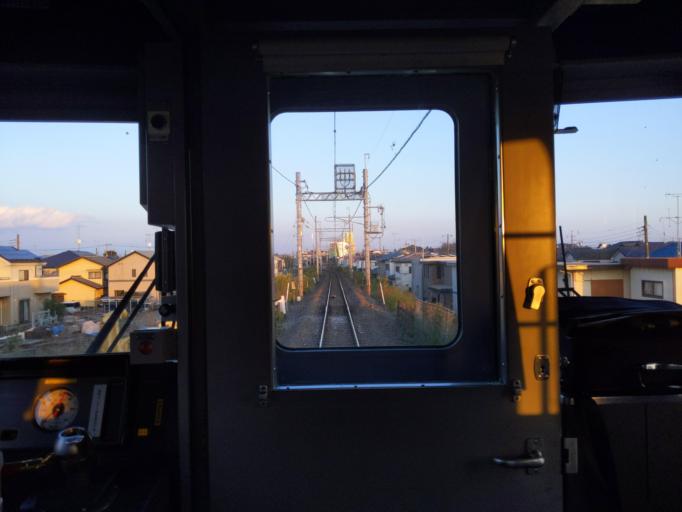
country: JP
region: Chiba
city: Noda
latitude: 35.9794
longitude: 139.8273
